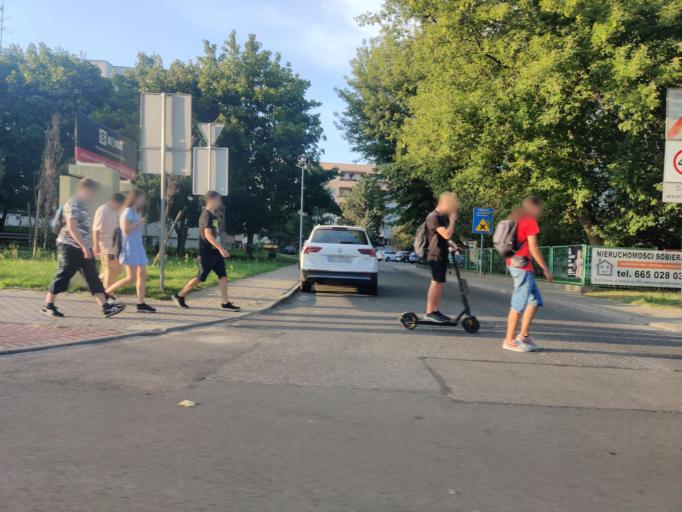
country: PL
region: Greater Poland Voivodeship
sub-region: Konin
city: Konin
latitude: 52.2322
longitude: 18.2566
